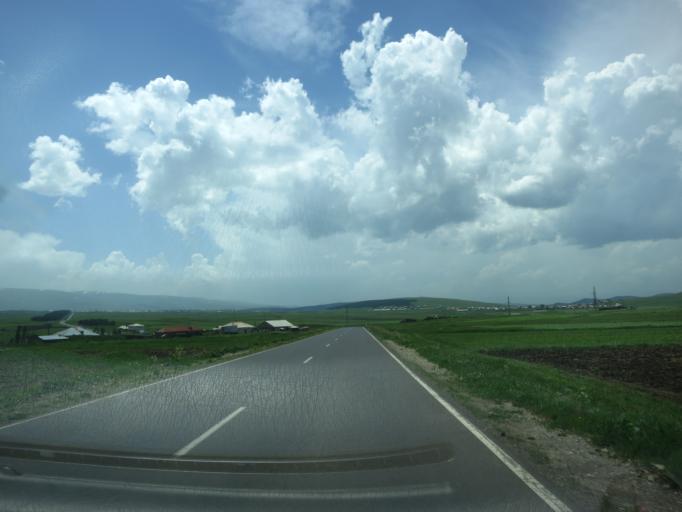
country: GE
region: Samtskhe-Javakheti
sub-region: Ninotsminda
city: Ninotsminda
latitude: 41.2952
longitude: 43.6497
